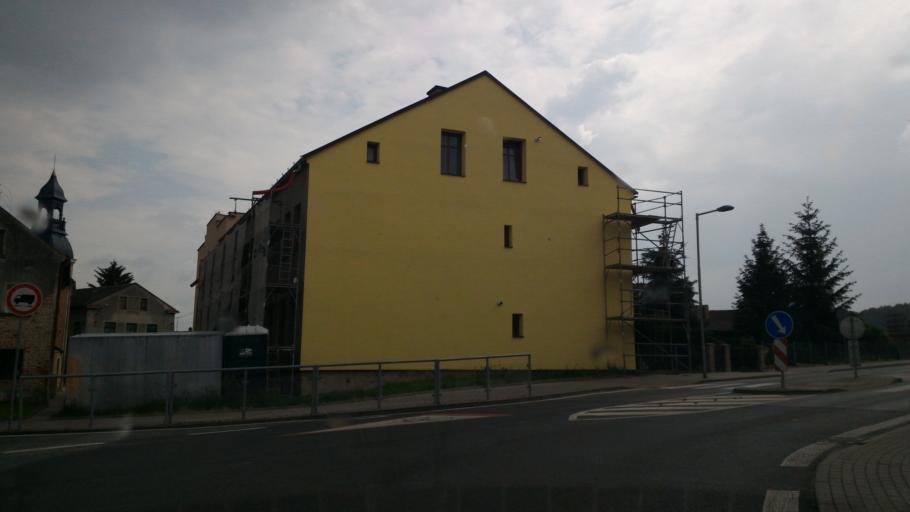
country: CZ
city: Hradek nad Nisou
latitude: 50.8497
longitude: 14.8442
